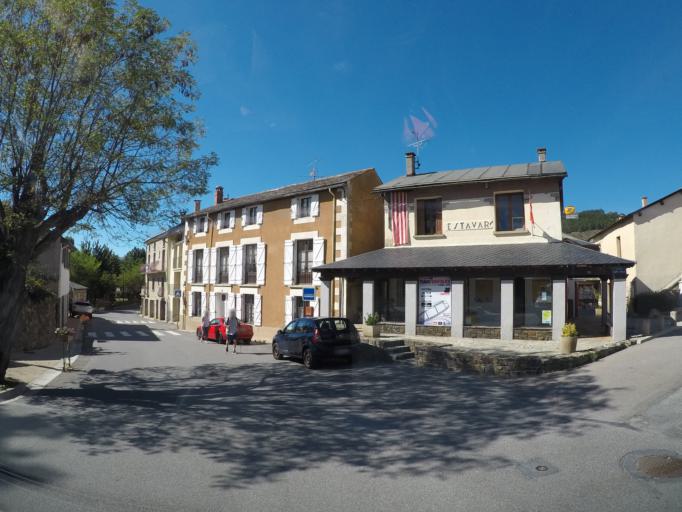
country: ES
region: Catalonia
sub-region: Provincia de Girona
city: Llivia
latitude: 42.4680
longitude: 1.9968
